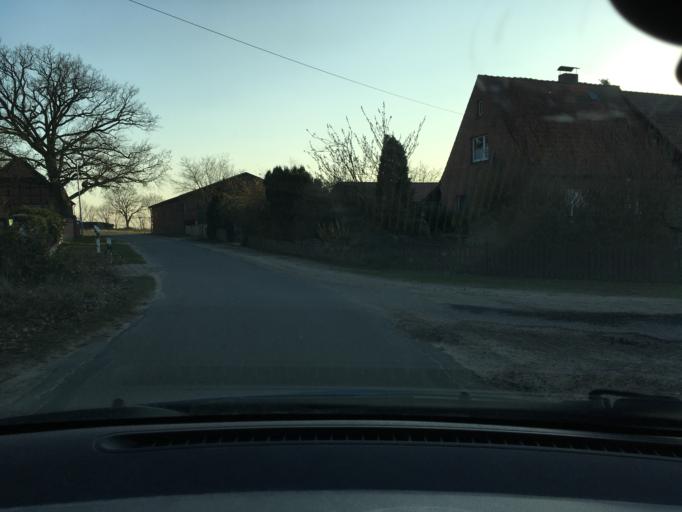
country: DE
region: Lower Saxony
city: Romstedt
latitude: 53.1501
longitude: 10.6620
